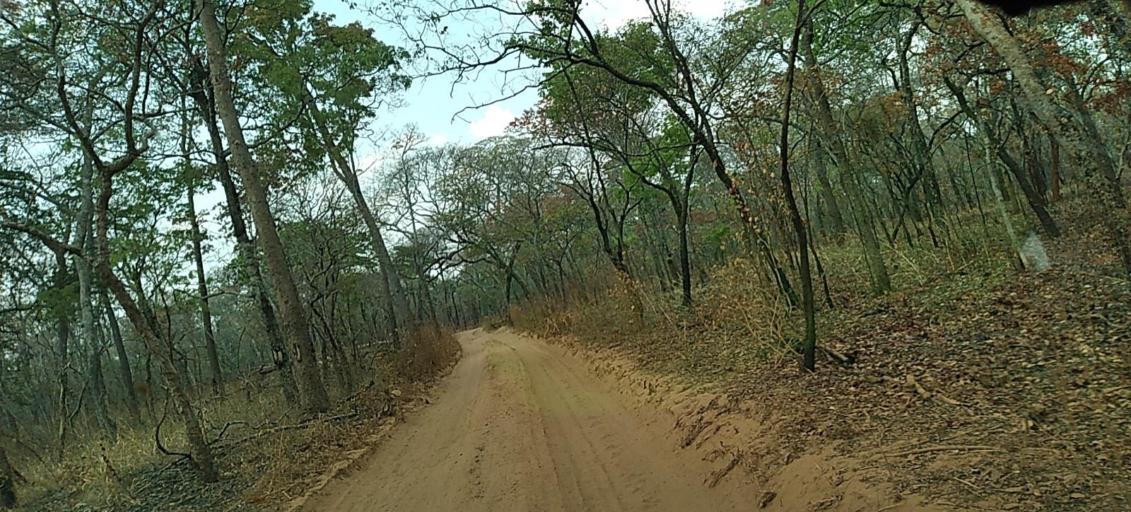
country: ZM
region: North-Western
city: Kabompo
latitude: -13.6143
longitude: 24.3719
